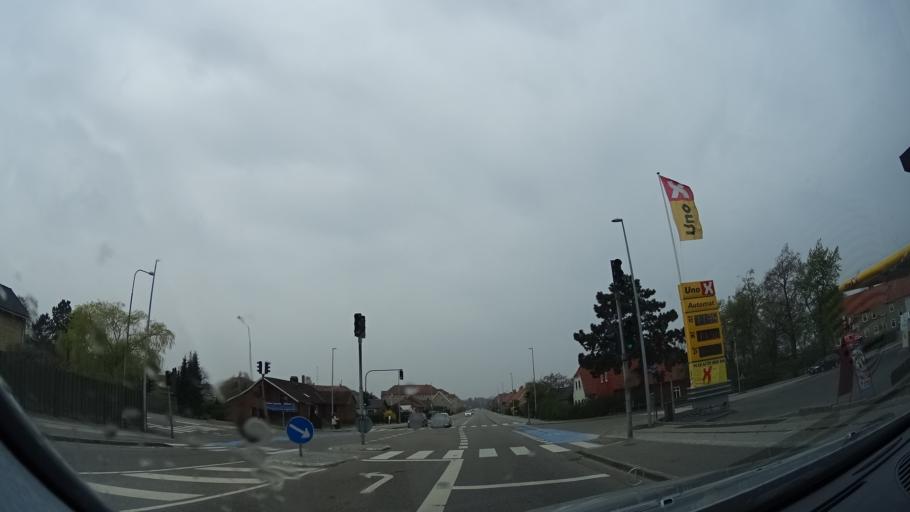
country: DK
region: Zealand
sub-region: Holbaek Kommune
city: Holbaek
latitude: 55.7144
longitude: 11.7404
